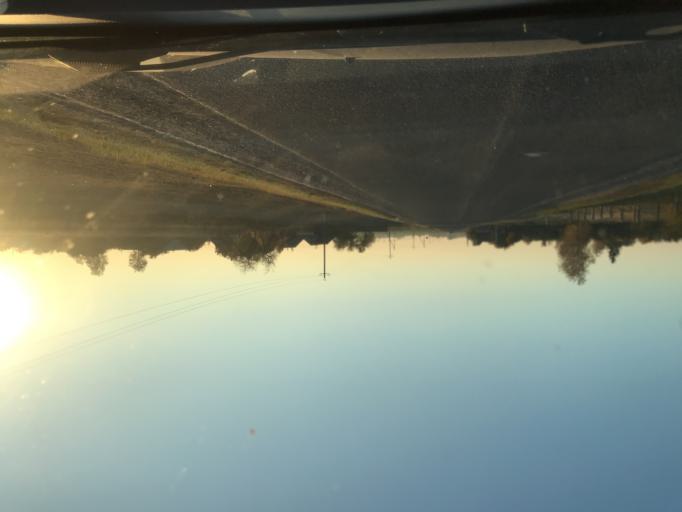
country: BY
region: Gomel
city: Brahin
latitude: 51.7946
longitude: 30.2612
